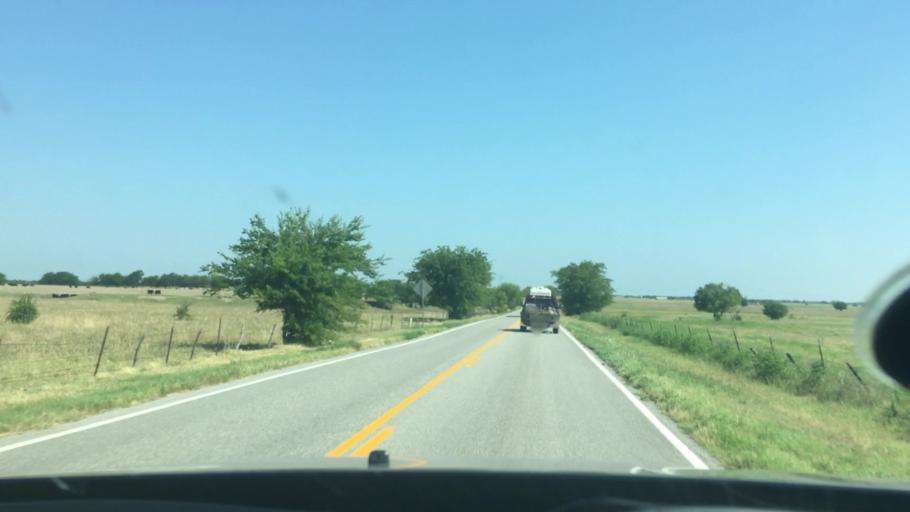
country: US
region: Oklahoma
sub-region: Johnston County
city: Tishomingo
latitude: 34.1528
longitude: -96.5060
